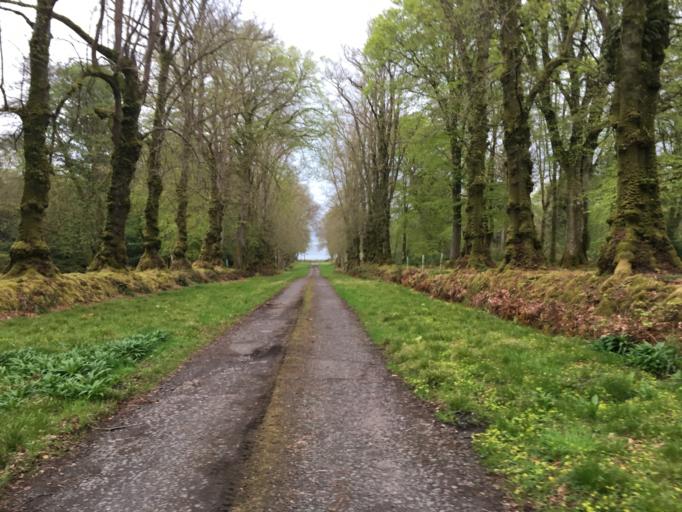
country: GB
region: Scotland
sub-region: Argyll and Bute
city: Rothesay
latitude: 55.7974
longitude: -5.0191
